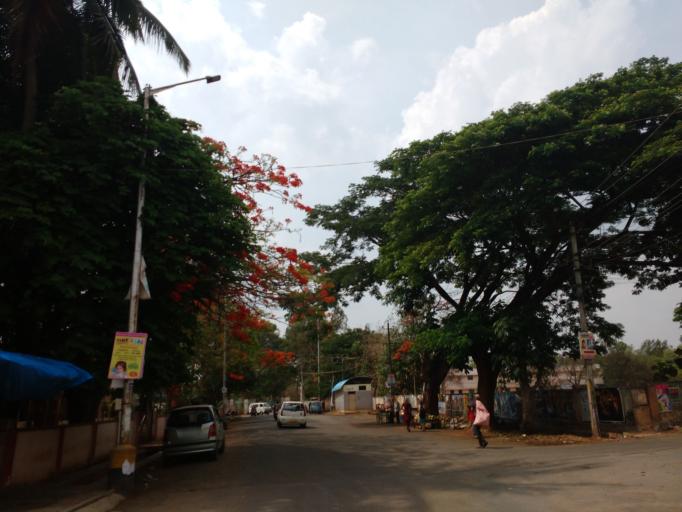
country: IN
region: Karnataka
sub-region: Hassan
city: Hassan
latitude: 13.0154
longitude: 76.1021
